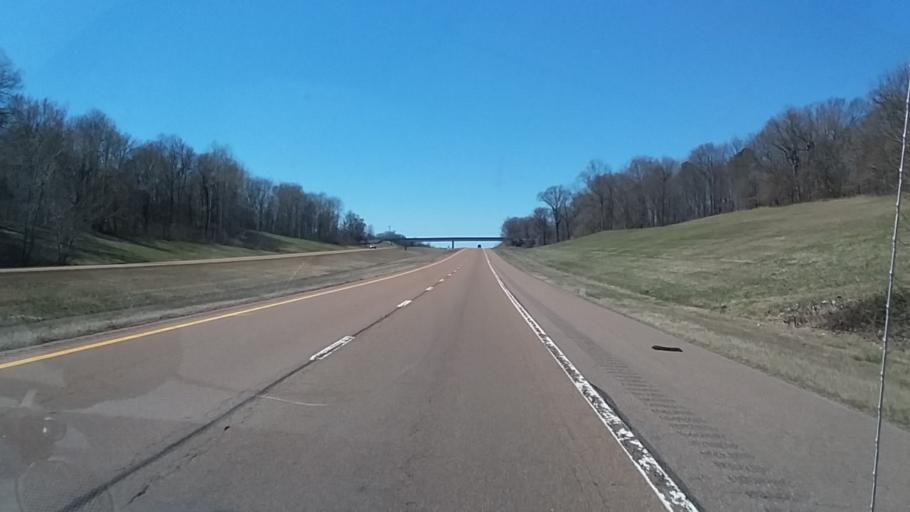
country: US
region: Tennessee
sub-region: Dyer County
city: Dyersburg
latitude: 36.0711
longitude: -89.4572
